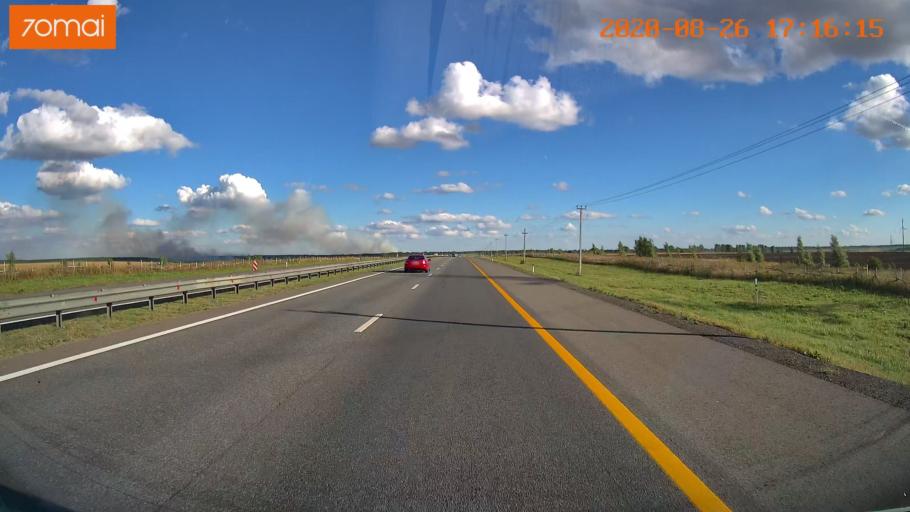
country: RU
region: Tula
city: Volovo
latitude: 53.6389
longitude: 38.0688
